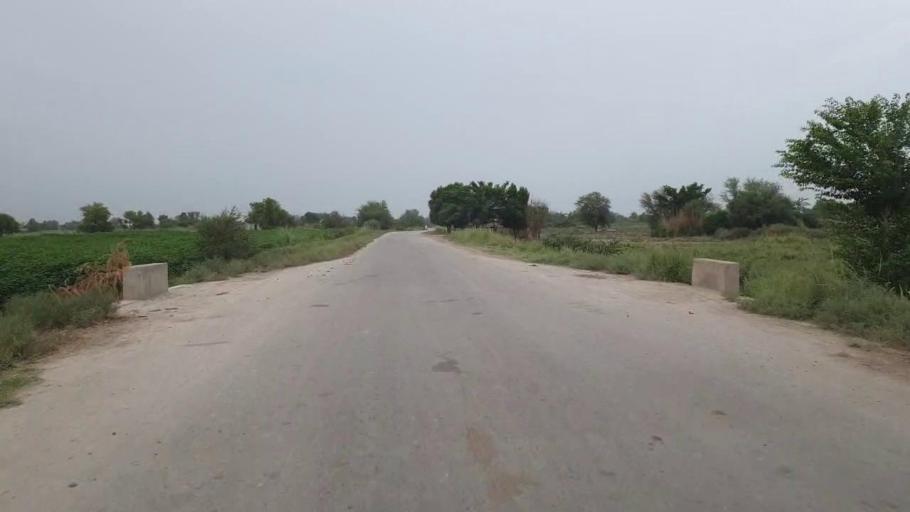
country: PK
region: Sindh
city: Bandhi
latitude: 26.5419
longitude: 68.2193
